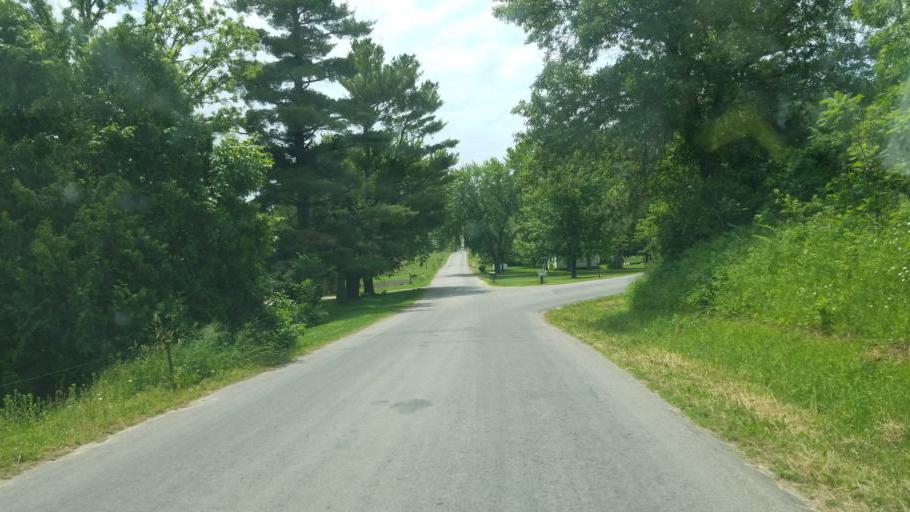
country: US
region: Wisconsin
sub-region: Monroe County
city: Cashton
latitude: 43.7235
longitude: -90.6671
